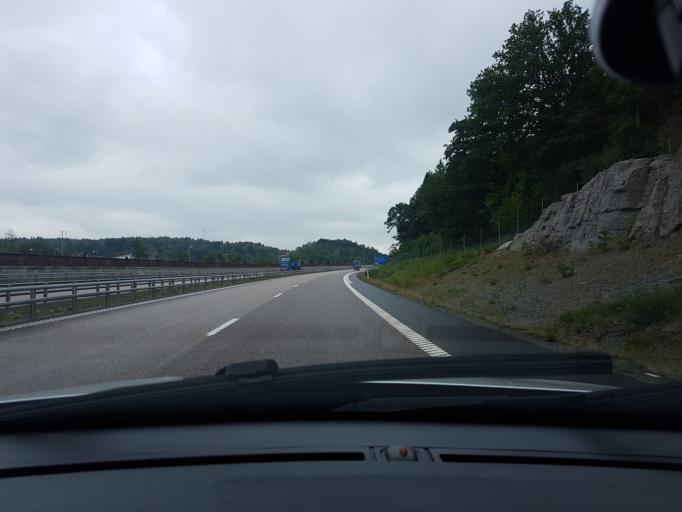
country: SE
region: Vaestra Goetaland
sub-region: Ale Kommun
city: Alafors
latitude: 57.9301
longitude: 12.0849
